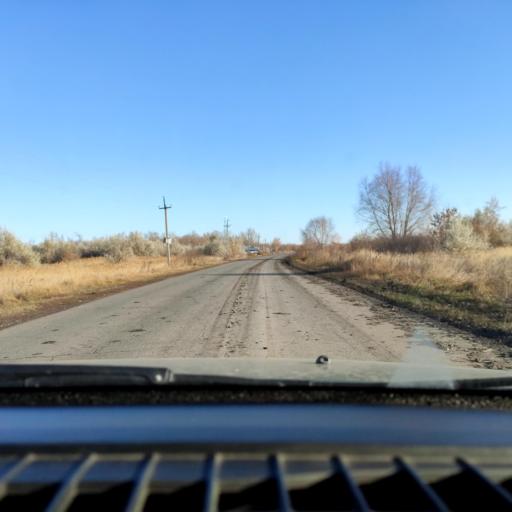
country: RU
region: Samara
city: Tol'yatti
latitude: 53.6368
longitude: 49.3096
